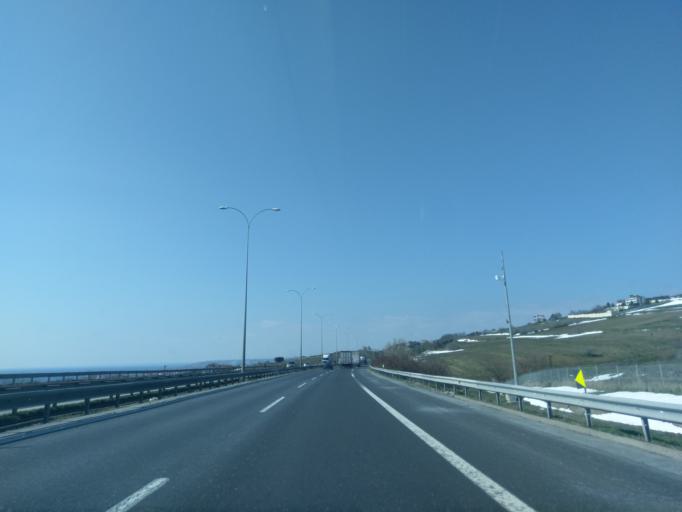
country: TR
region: Istanbul
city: Celaliye
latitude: 41.0516
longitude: 28.4351
